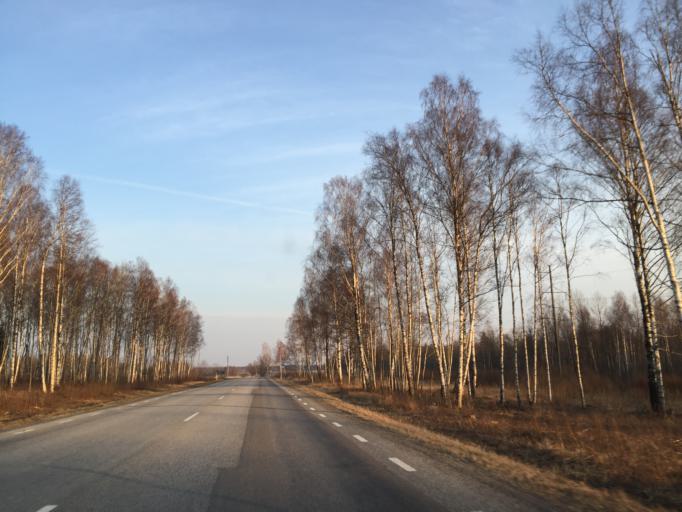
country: EE
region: Laeaene
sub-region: Lihula vald
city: Lihula
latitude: 58.5414
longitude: 24.0076
